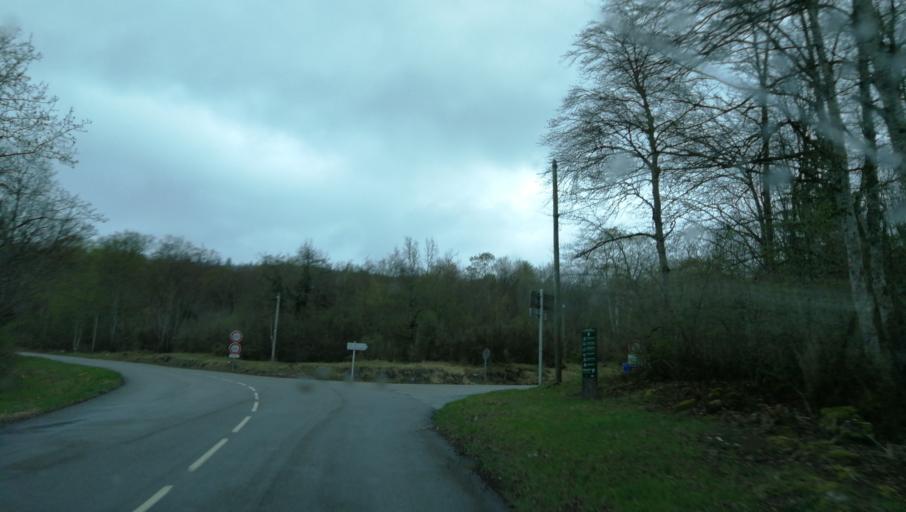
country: FR
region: Rhone-Alpes
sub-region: Departement de la Drome
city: Saint-Laurent-en-Royans
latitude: 45.0034
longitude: 5.3201
